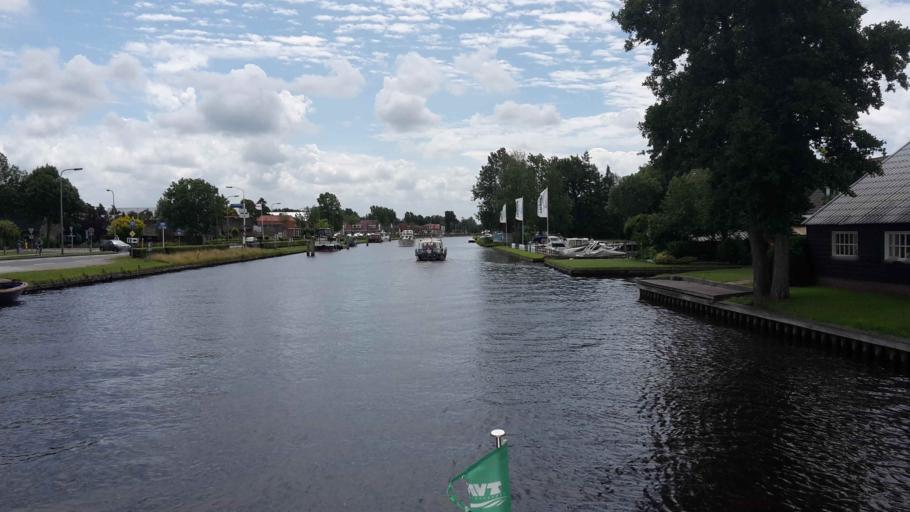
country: NL
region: Overijssel
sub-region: Gemeente Steenwijkerland
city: Giethoorn
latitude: 52.7212
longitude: 6.0772
